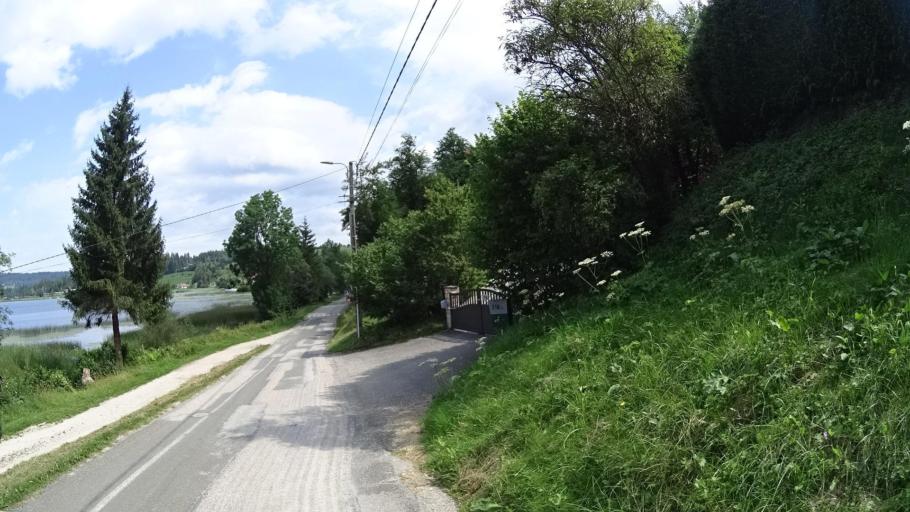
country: FR
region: Franche-Comte
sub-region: Departement du Doubs
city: Les Fourgs
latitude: 46.8306
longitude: 6.3379
